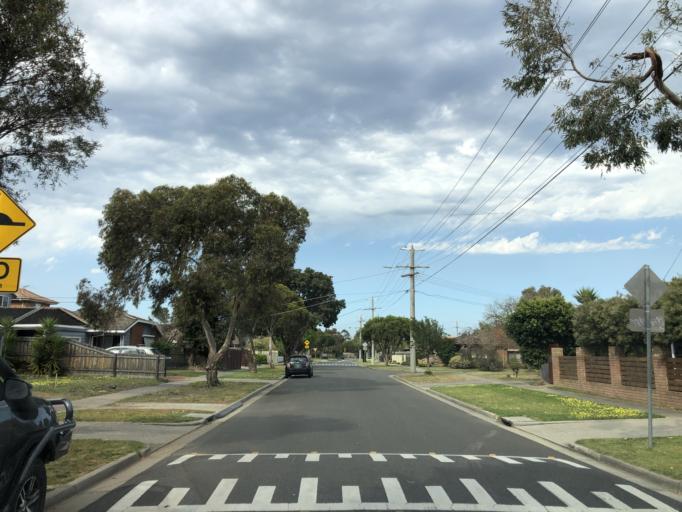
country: AU
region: Victoria
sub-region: Kingston
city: Carrum
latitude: -38.0870
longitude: 145.1359
